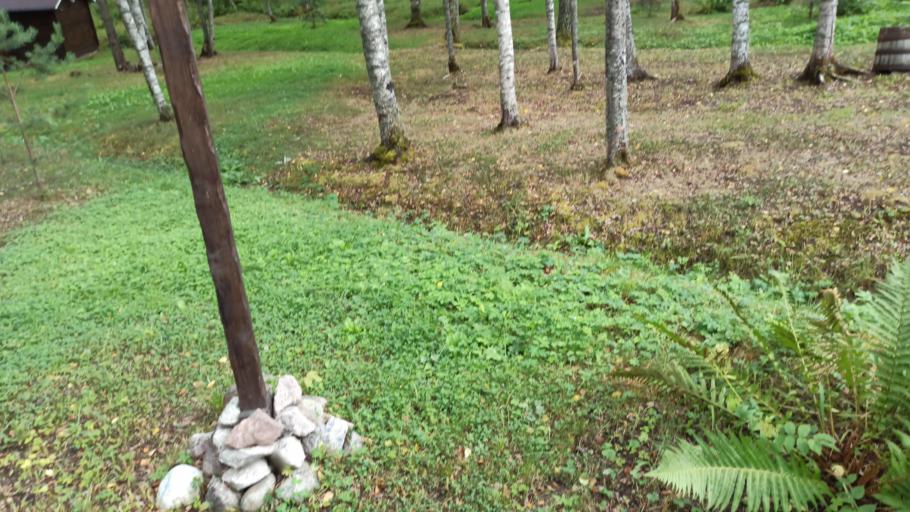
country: RU
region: Republic of Karelia
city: Lakhdenpokh'ya
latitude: 61.4402
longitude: 30.2339
